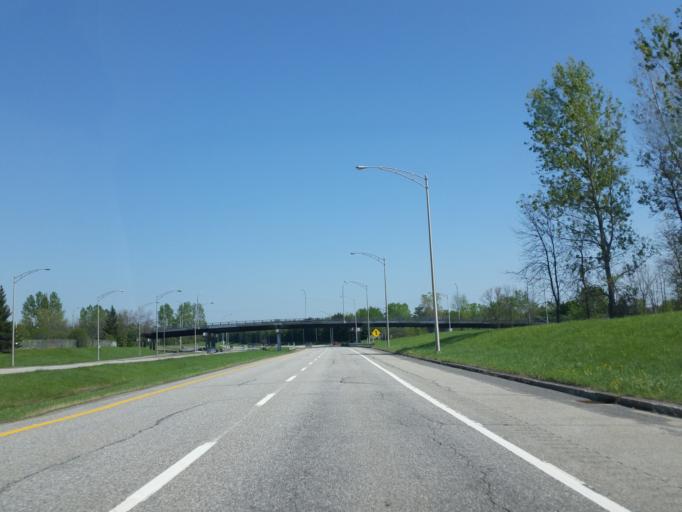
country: CA
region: Quebec
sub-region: Outaouais
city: Gatineau
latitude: 45.4751
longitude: -75.7795
